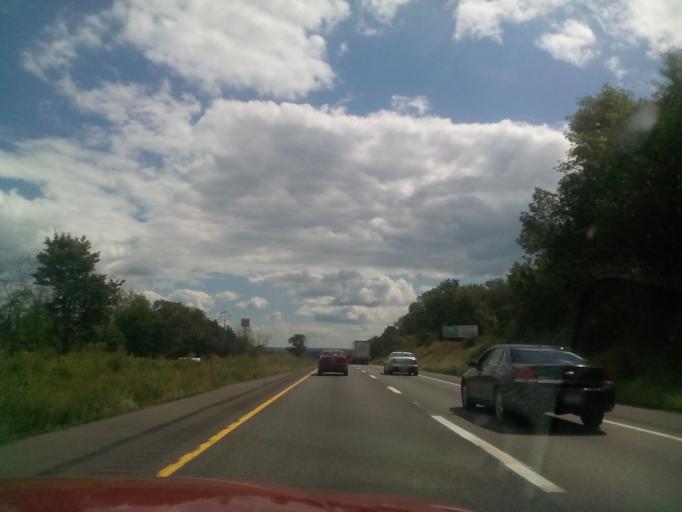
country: US
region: Pennsylvania
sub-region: Monroe County
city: Tannersville
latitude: 41.0441
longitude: -75.3142
